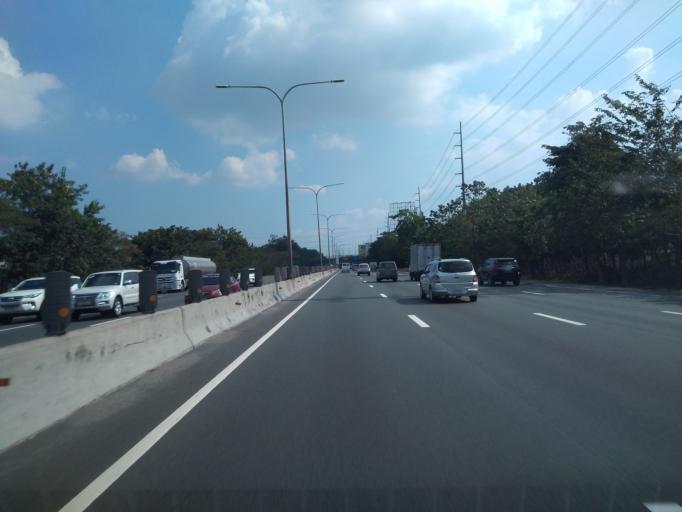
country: PH
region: Calabarzon
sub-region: Province of Laguna
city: Magsaysay
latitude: 14.3360
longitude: 121.0528
